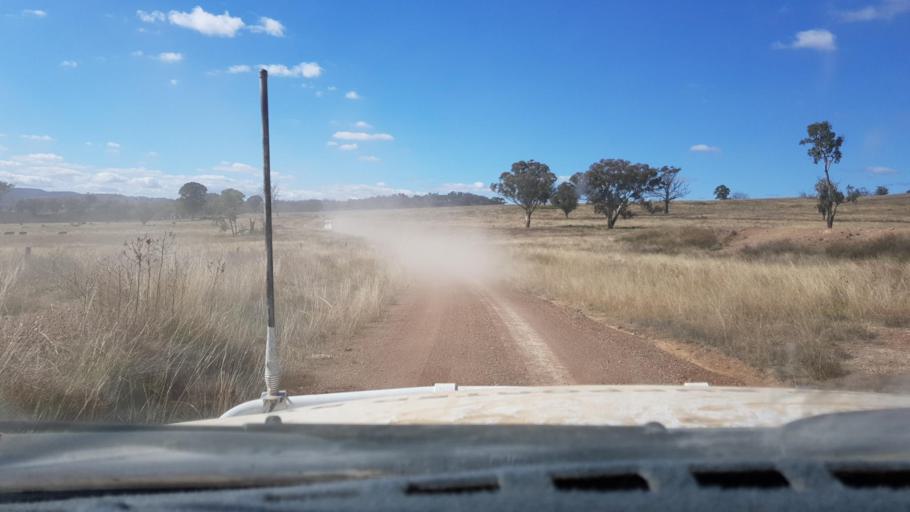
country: AU
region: New South Wales
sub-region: Tamworth Municipality
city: Manilla
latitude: -30.4394
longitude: 150.8530
